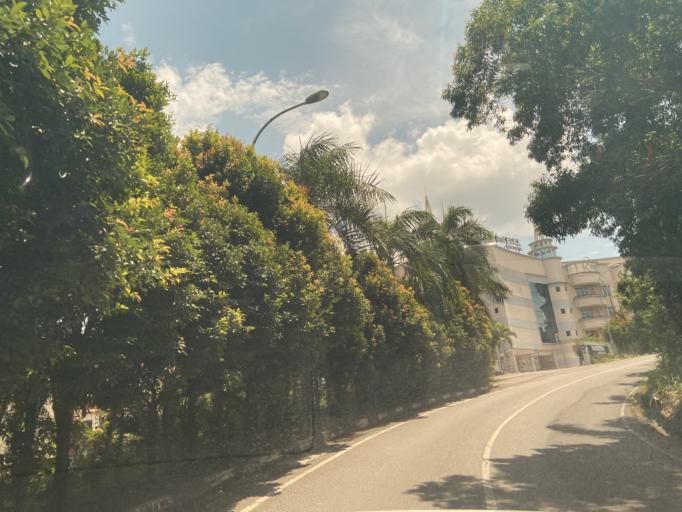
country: SG
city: Singapore
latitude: 1.1522
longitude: 104.0083
